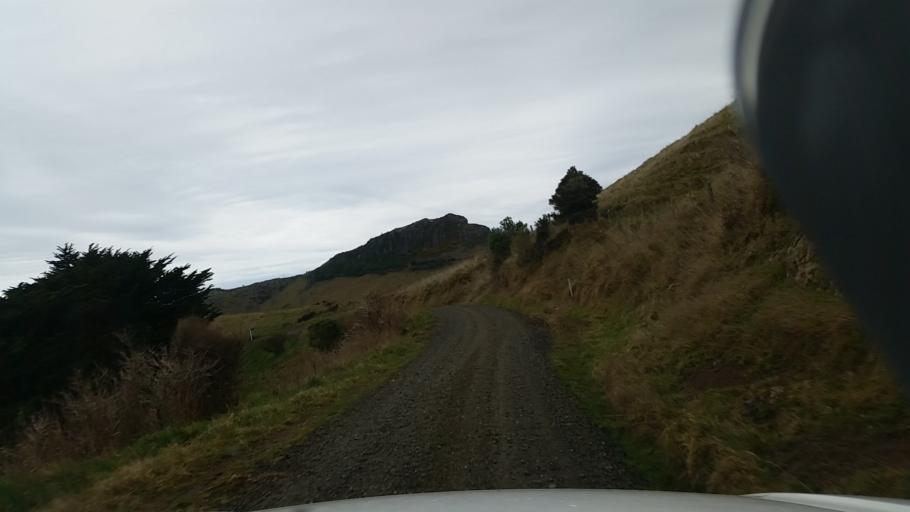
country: NZ
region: Canterbury
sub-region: Christchurch City
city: Christchurch
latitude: -43.7375
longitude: 173.0291
